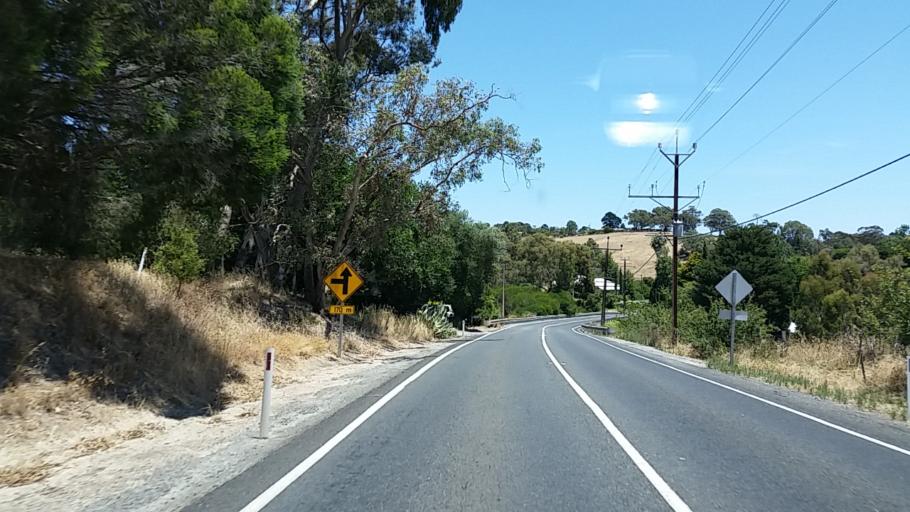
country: AU
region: South Australia
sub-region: Tea Tree Gully
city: Golden Grove
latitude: -34.8247
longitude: 138.7816
